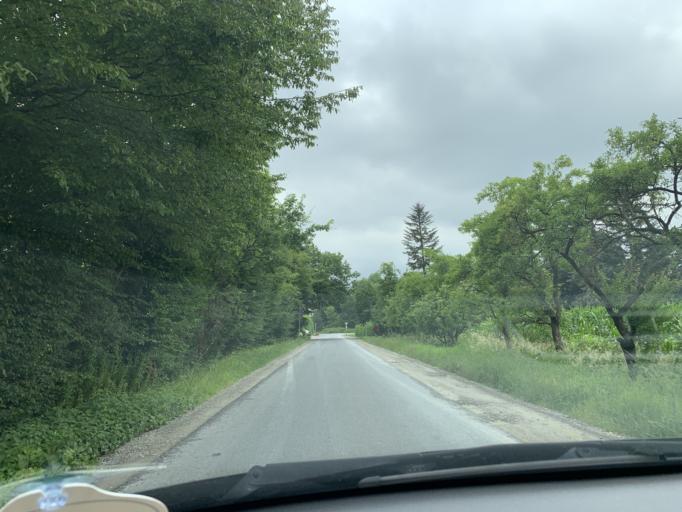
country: DE
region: North Rhine-Westphalia
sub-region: Regierungsbezirk Munster
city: Ennigerloh
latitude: 51.8320
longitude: 8.0720
